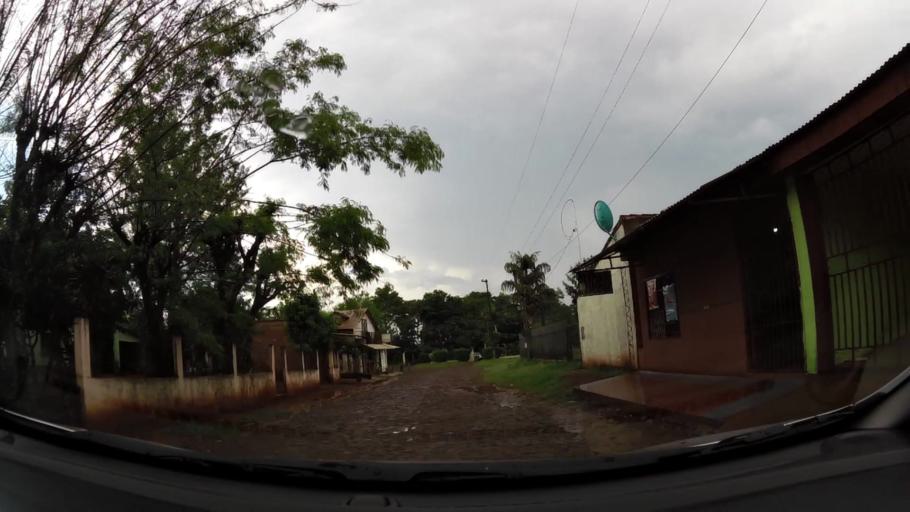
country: PY
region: Alto Parana
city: Presidente Franco
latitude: -25.5484
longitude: -54.6520
